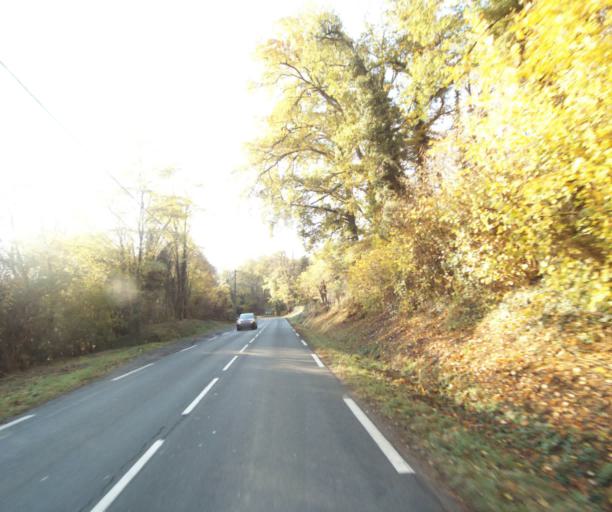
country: FR
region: Auvergne
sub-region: Departement du Puy-de-Dome
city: Nohanent
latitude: 45.8091
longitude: 3.0499
